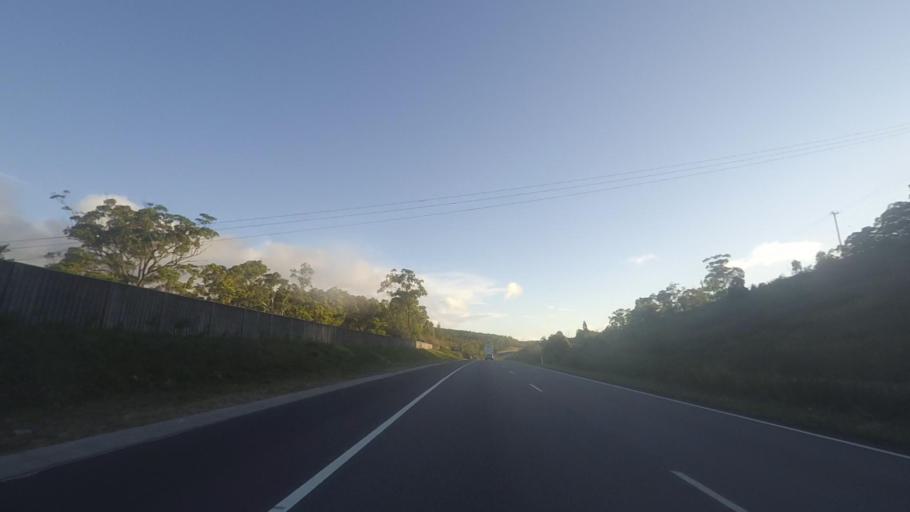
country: AU
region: New South Wales
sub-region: Great Lakes
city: Bulahdelah
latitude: -32.5075
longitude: 152.2113
